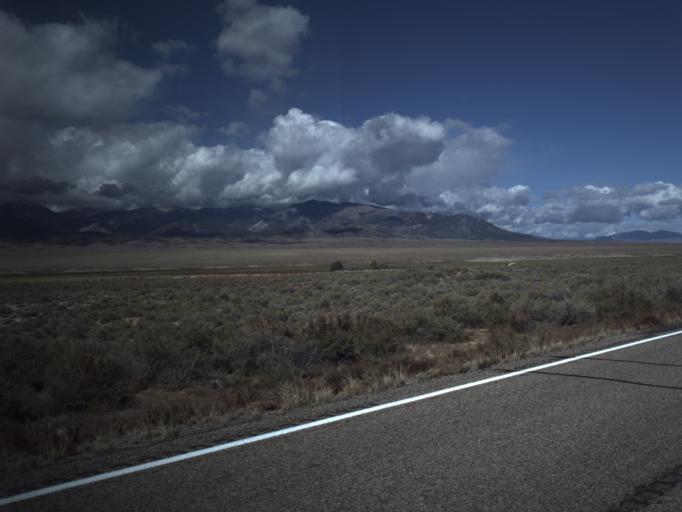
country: US
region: Nevada
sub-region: White Pine County
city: McGill
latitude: 38.8197
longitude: -113.9859
